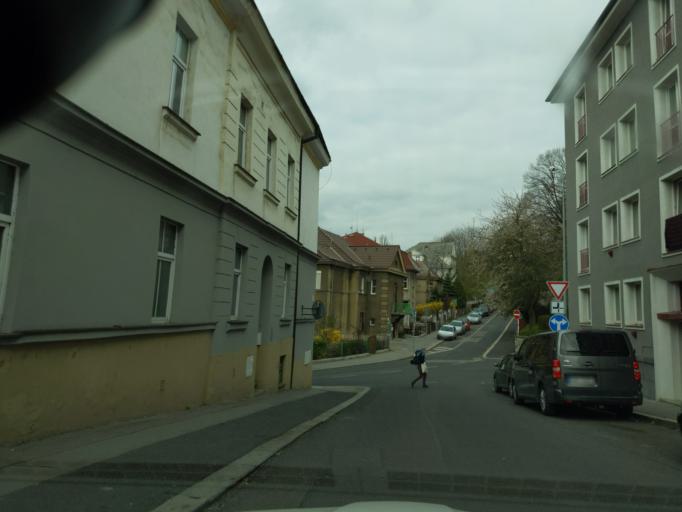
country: CZ
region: Ustecky
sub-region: Okres Usti nad Labem
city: Usti nad Labem
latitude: 50.6676
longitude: 14.0305
